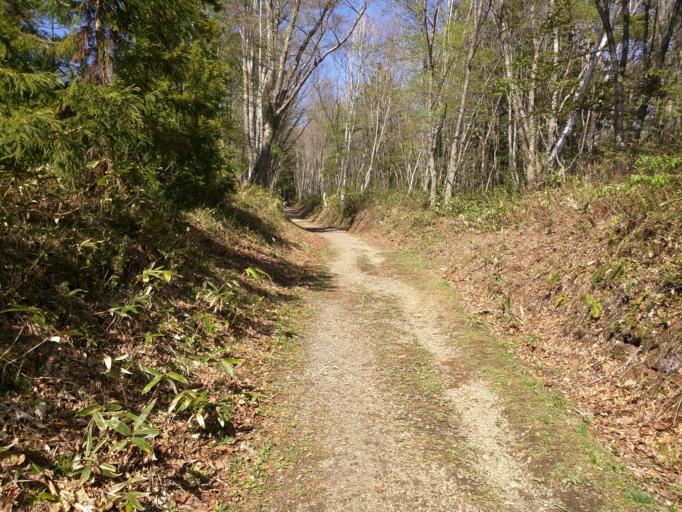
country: JP
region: Nagano
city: Nagano-shi
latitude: 36.7342
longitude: 138.0790
